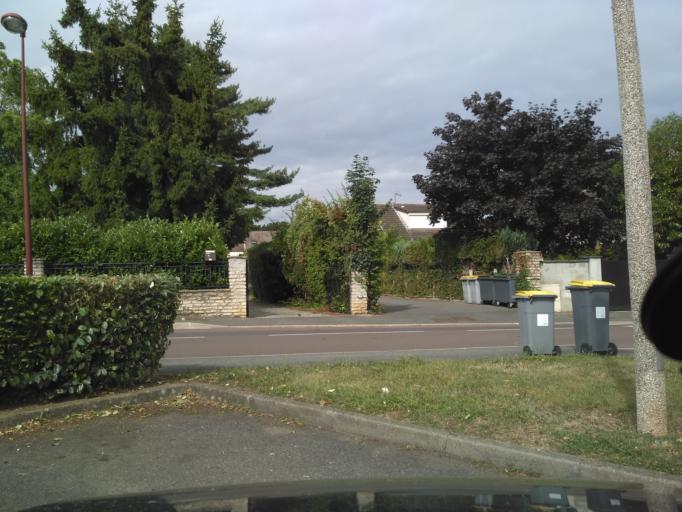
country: FR
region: Ile-de-France
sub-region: Departement de Seine-et-Marne
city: Cesson
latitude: 48.5636
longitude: 2.6132
